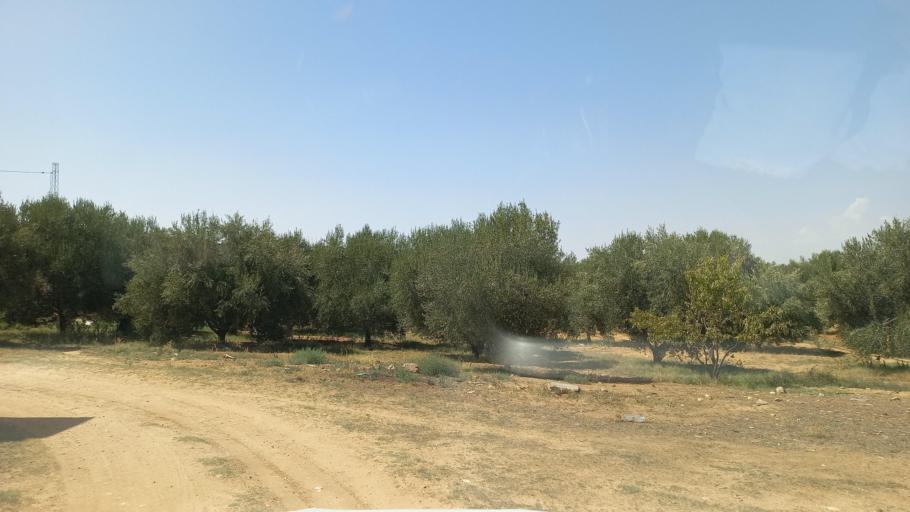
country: TN
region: Al Qasrayn
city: Kasserine
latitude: 35.2368
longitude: 9.0286
